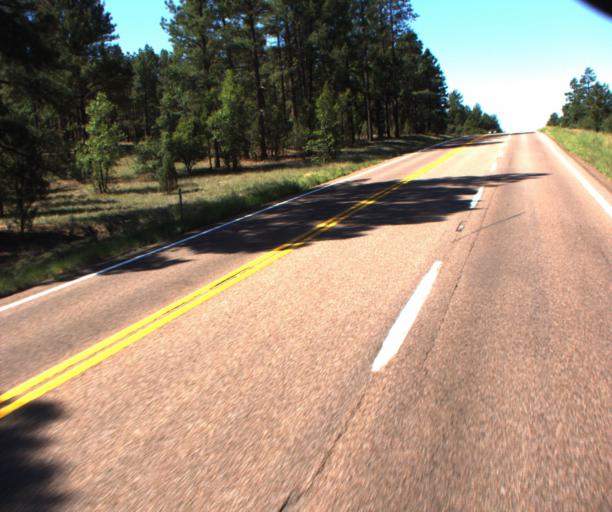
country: US
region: Arizona
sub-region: Navajo County
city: Linden
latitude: 34.0930
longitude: -110.1739
